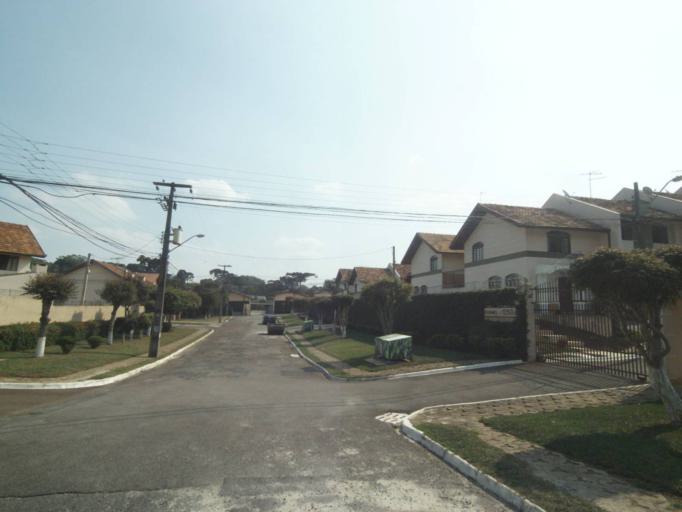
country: BR
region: Parana
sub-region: Sao Jose Dos Pinhais
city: Sao Jose dos Pinhais
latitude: -25.5149
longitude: -49.2499
